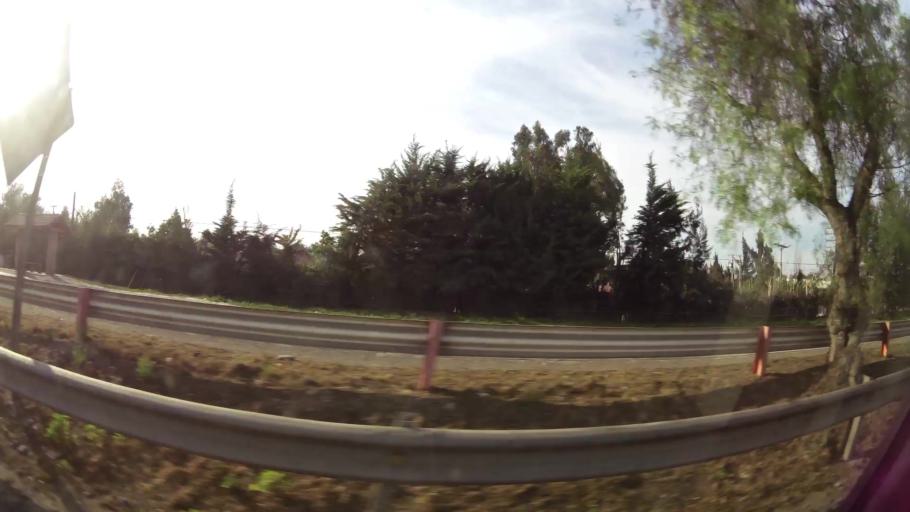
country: CL
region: Santiago Metropolitan
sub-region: Provincia de Talagante
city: Penaflor
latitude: -33.5831
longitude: -70.8314
